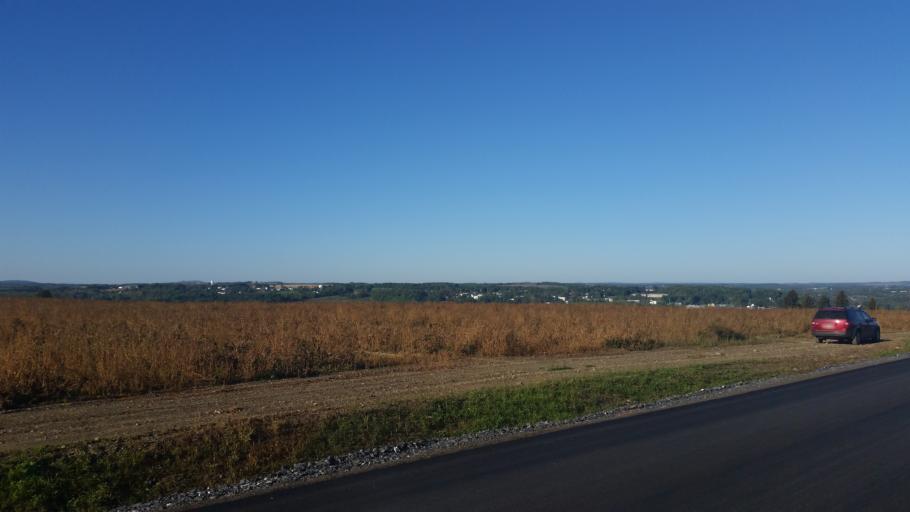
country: US
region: Maine
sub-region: Aroostook County
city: Caribou
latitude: 46.8541
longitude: -67.9869
